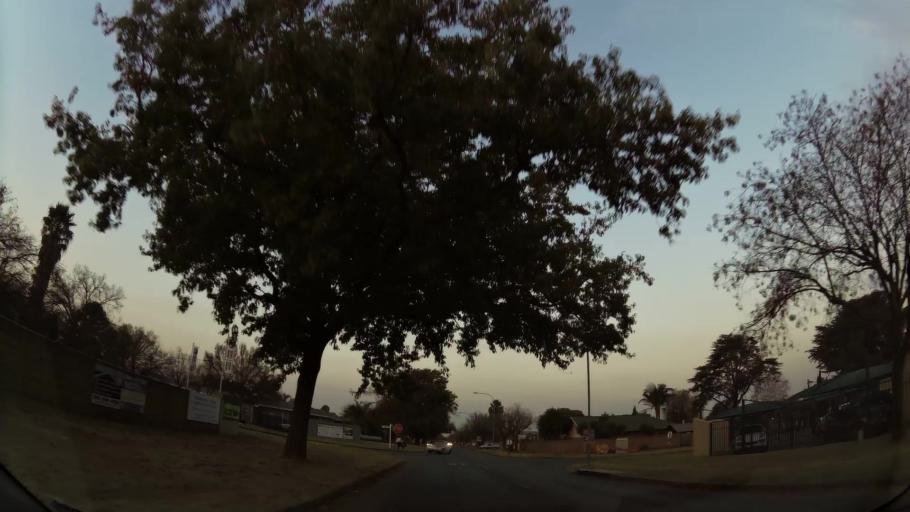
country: ZA
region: Gauteng
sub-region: Ekurhuleni Metropolitan Municipality
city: Benoni
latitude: -26.1642
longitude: 28.3186
